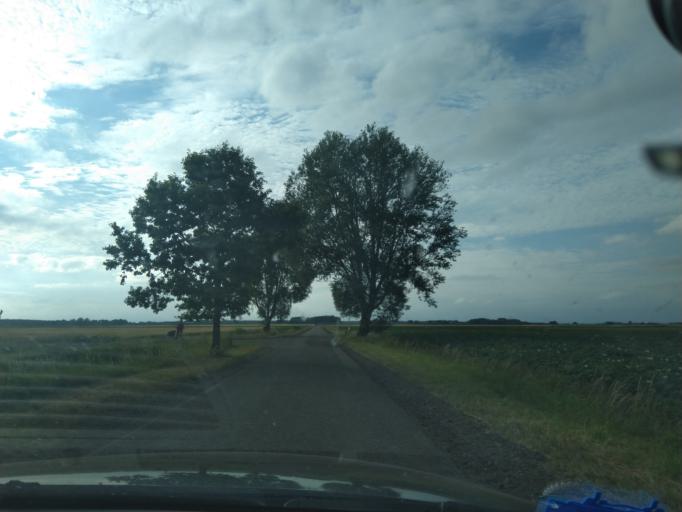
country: NL
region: Groningen
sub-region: Gemeente Vlagtwedde
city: Vlagtwedde
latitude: 53.0790
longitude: 7.1135
